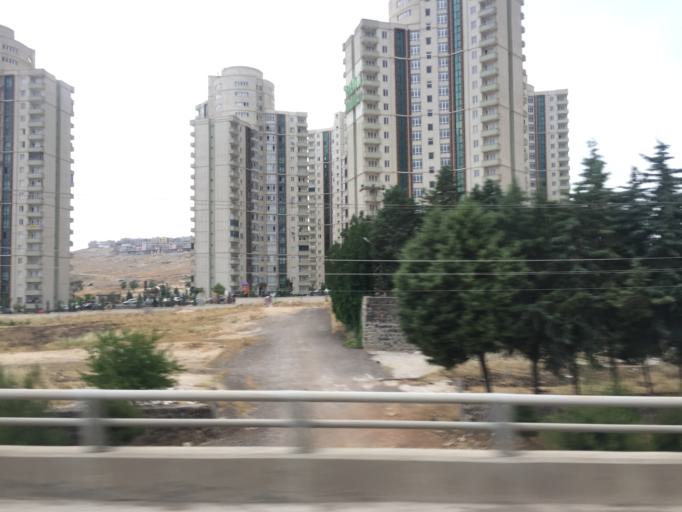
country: TR
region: Gaziantep
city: Gaziantep
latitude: 37.0381
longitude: 37.4236
